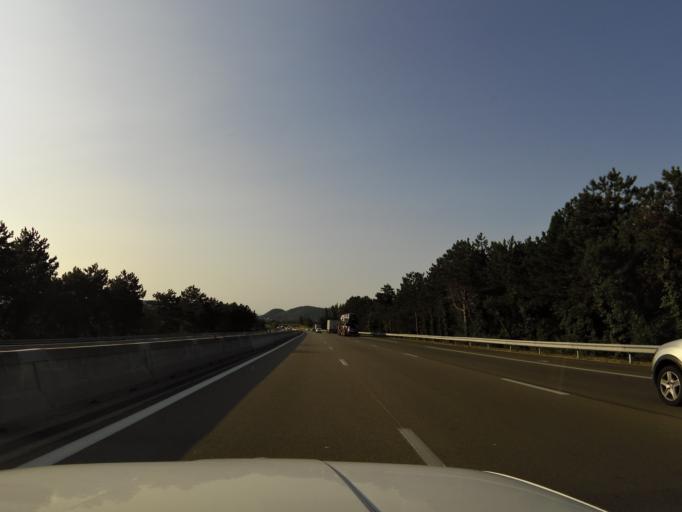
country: FR
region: Rhone-Alpes
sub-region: Departement de la Drome
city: Montboucher-sur-Jabron
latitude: 44.5632
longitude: 4.8109
